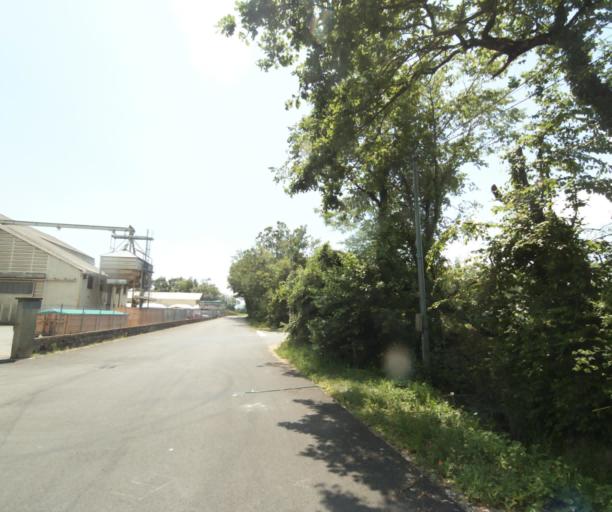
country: FR
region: Rhone-Alpes
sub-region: Departement de la Haute-Savoie
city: Douvaine
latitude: 46.3207
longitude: 6.2949
